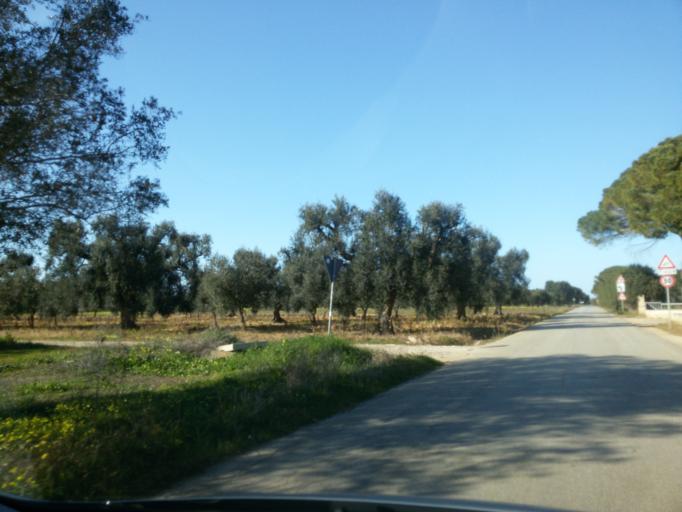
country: IT
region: Apulia
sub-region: Provincia di Brindisi
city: Mesagne
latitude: 40.6567
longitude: 17.8240
